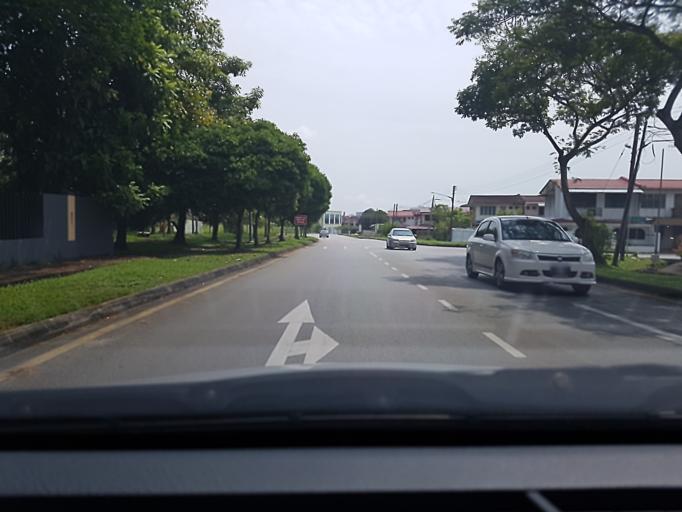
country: MY
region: Sarawak
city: Kuching
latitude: 1.5111
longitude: 110.3624
